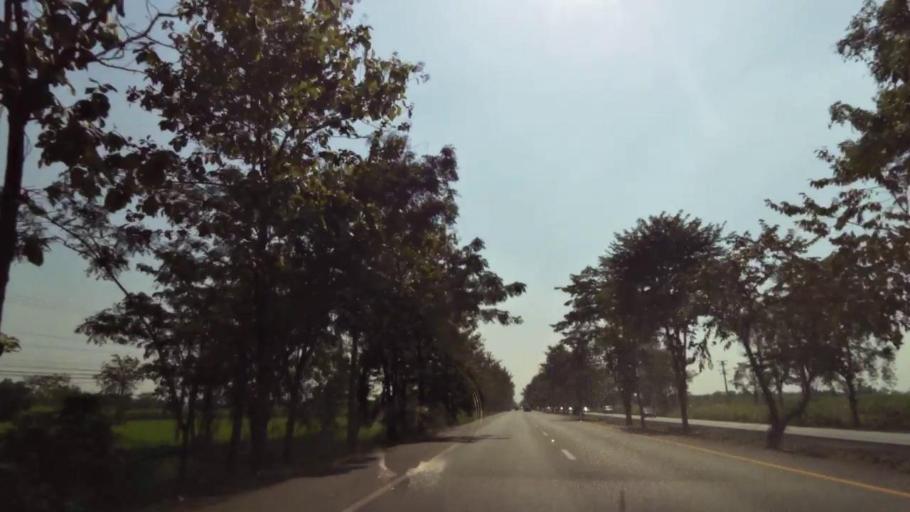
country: TH
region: Phichit
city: Bueng Na Rang
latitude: 16.0832
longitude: 100.1247
